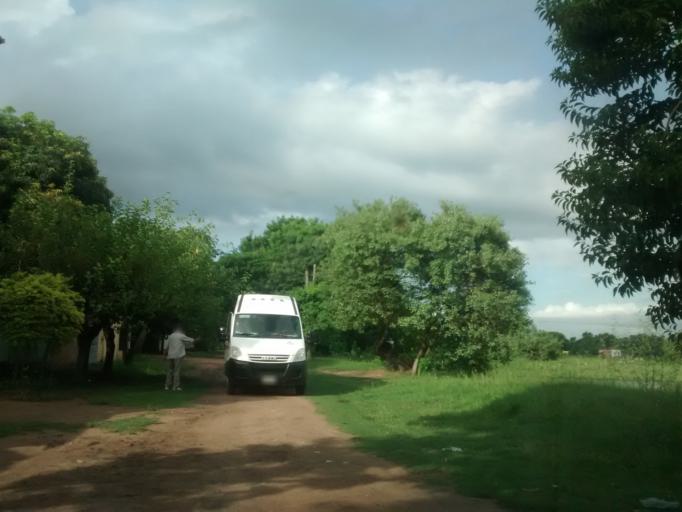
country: AR
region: Chaco
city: Puerto Tirol
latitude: -27.3753
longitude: -59.0883
